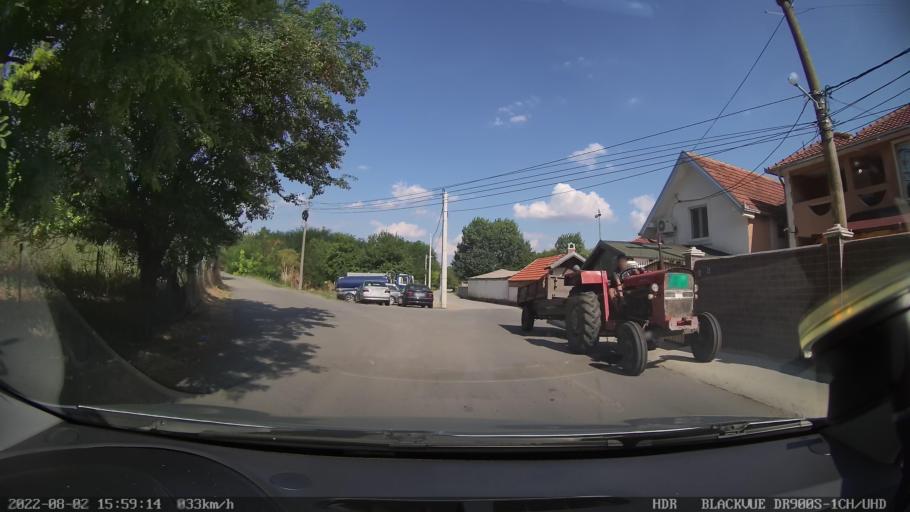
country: RS
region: Central Serbia
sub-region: Belgrade
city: Surcin
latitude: 44.7894
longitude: 20.2756
